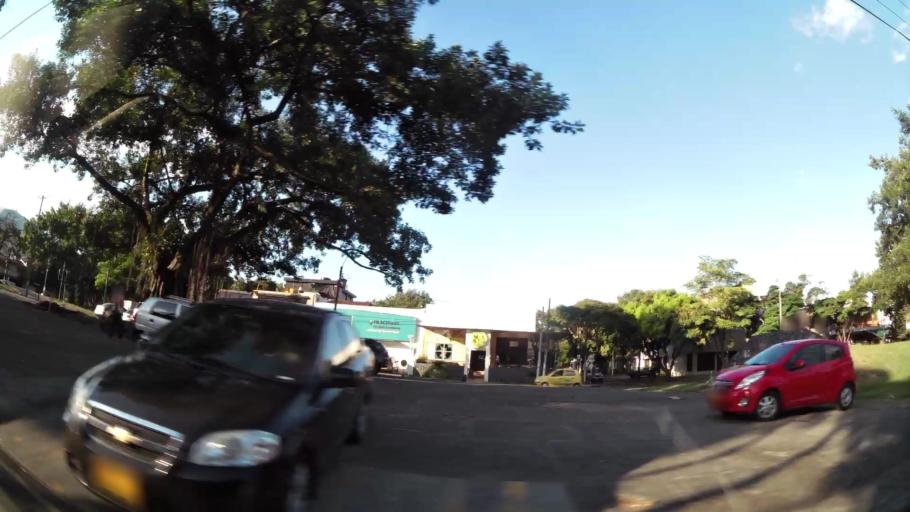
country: CO
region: Valle del Cauca
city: Cali
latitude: 3.4803
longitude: -76.5215
